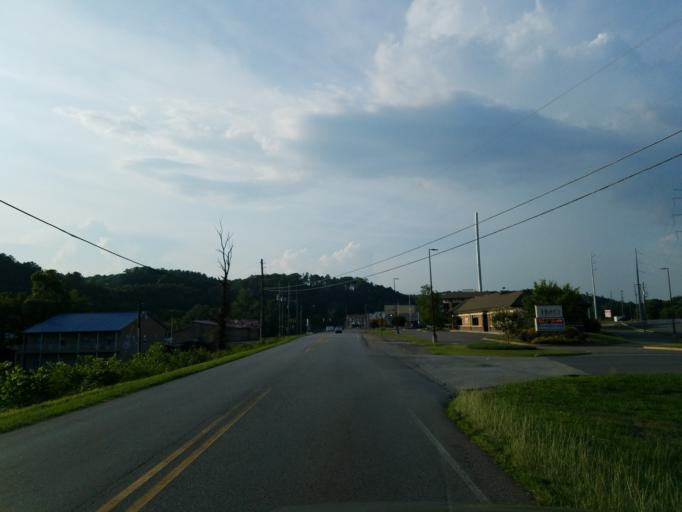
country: US
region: Georgia
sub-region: Gilmer County
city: Ellijay
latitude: 34.6813
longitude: -84.4910
